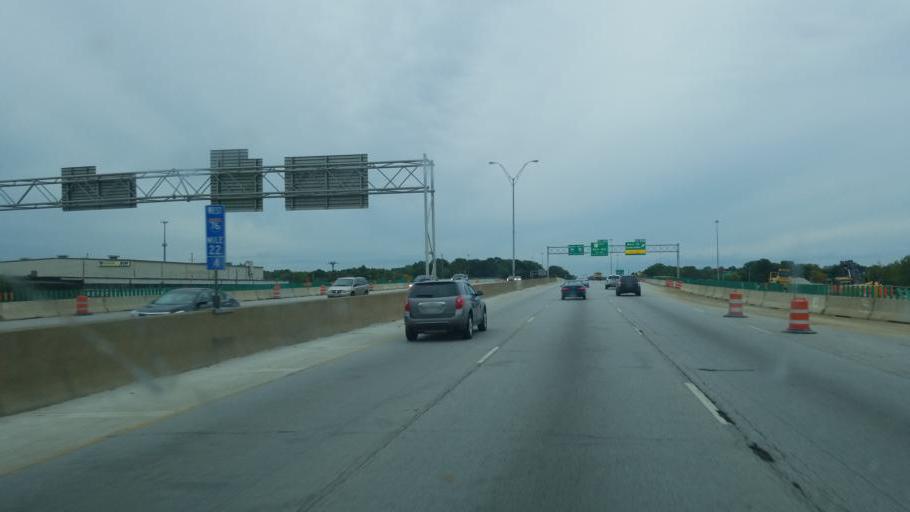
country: US
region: Ohio
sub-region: Summit County
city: Akron
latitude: 41.0626
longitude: -81.5218
